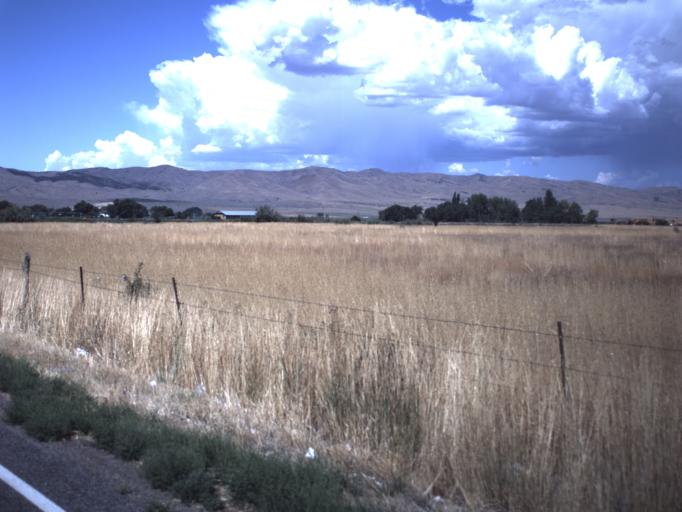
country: US
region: Utah
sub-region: Juab County
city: Nephi
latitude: 39.7100
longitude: -111.8460
